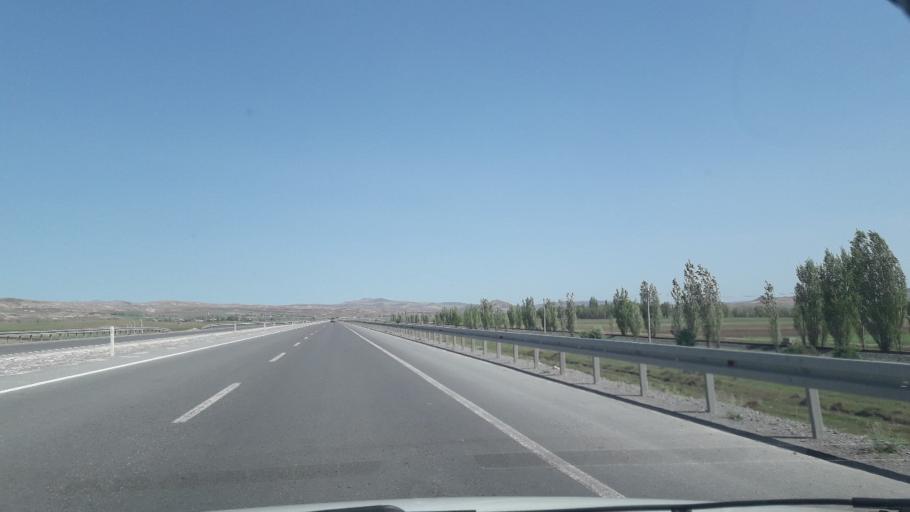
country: TR
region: Sivas
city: Ulas
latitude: 39.4762
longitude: 37.0127
